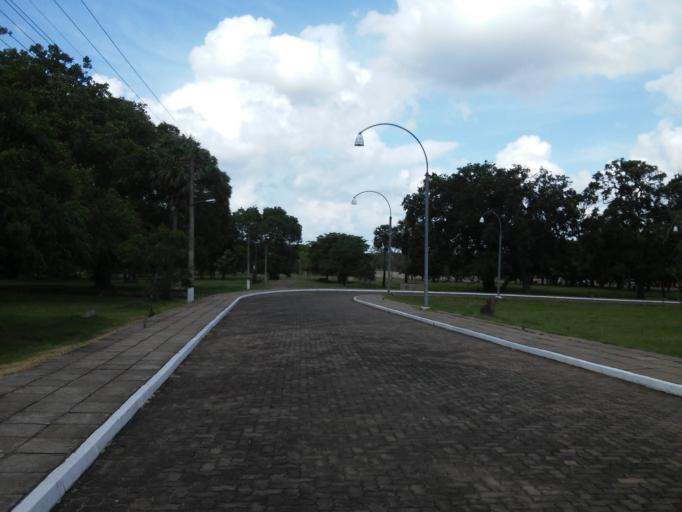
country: LK
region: North Central
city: Anuradhapura
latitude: 8.3454
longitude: 80.3984
